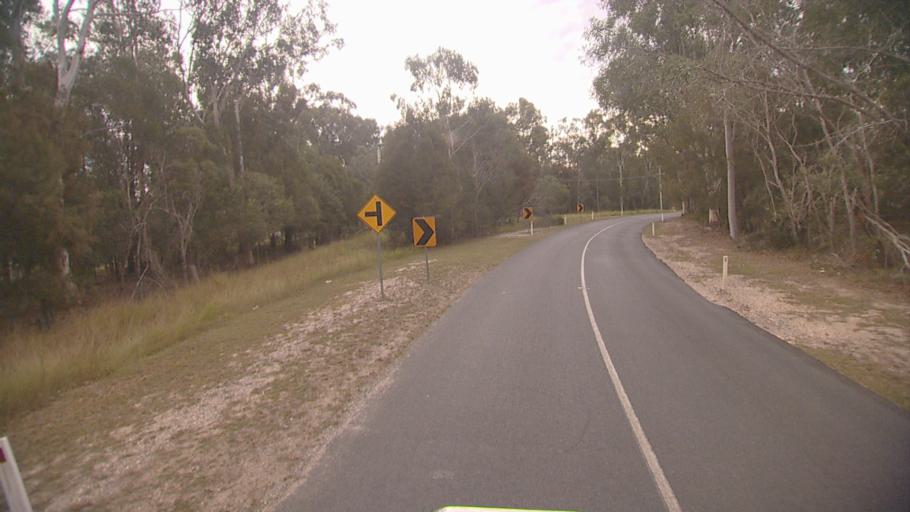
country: AU
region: Queensland
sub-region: Logan
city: Chambers Flat
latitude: -27.7767
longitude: 153.1155
